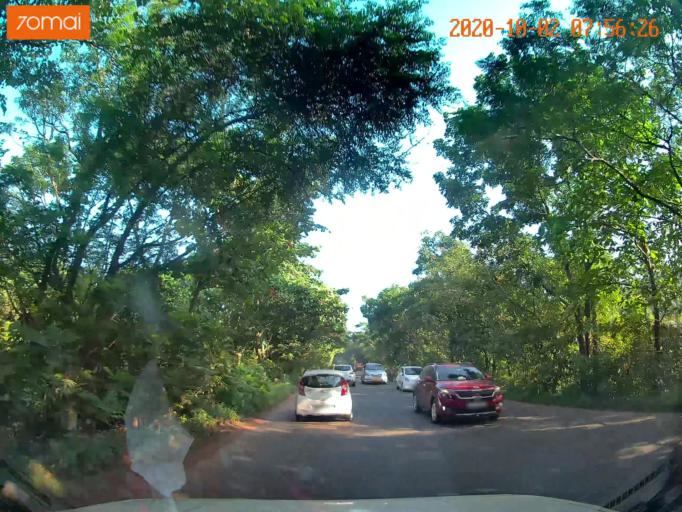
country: IN
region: Kerala
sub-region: Kozhikode
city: Ferokh
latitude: 11.1910
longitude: 75.8695
